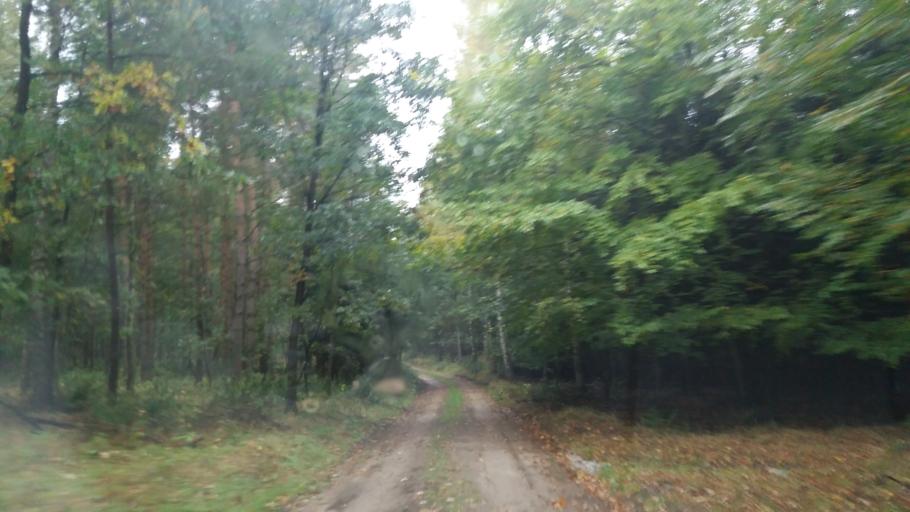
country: PL
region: West Pomeranian Voivodeship
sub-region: Powiat choszczenski
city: Pelczyce
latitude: 53.0752
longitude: 15.2674
